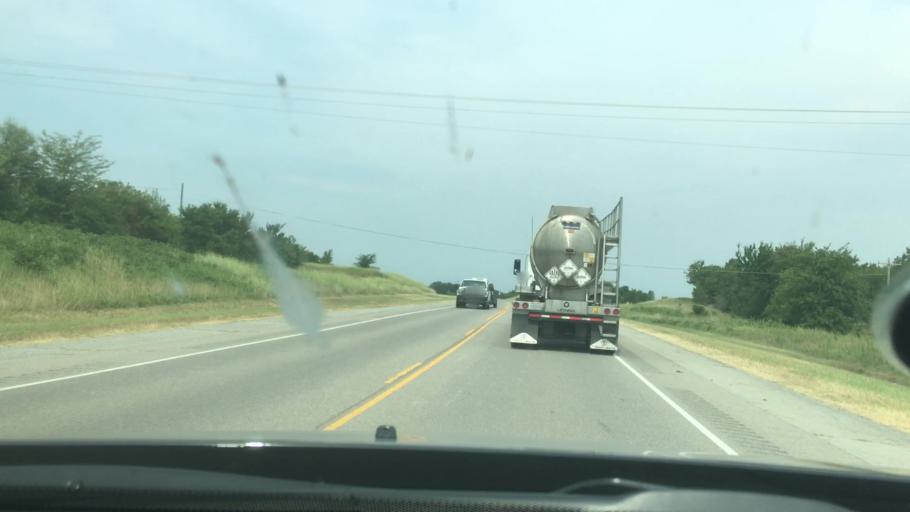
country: US
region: Oklahoma
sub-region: Pontotoc County
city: Ada
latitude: 34.6421
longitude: -96.4921
